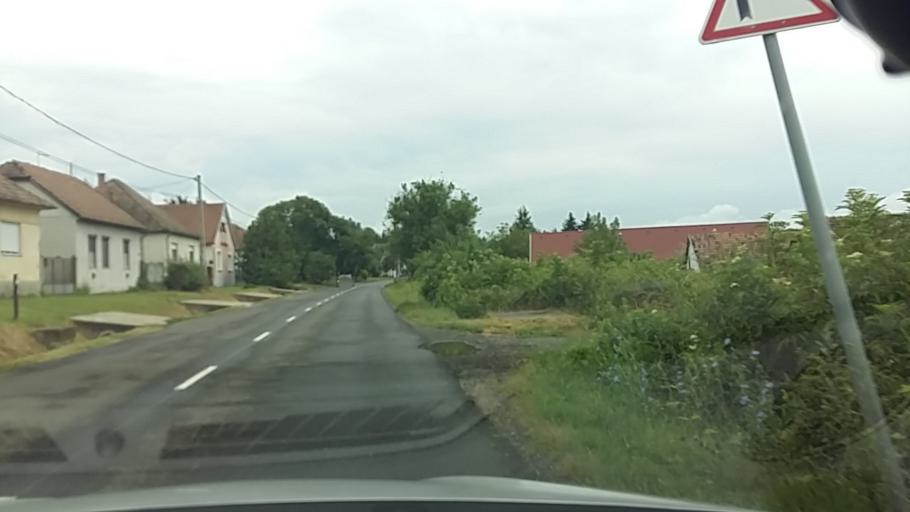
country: HU
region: Pest
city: Szob
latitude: 47.8442
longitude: 18.8256
